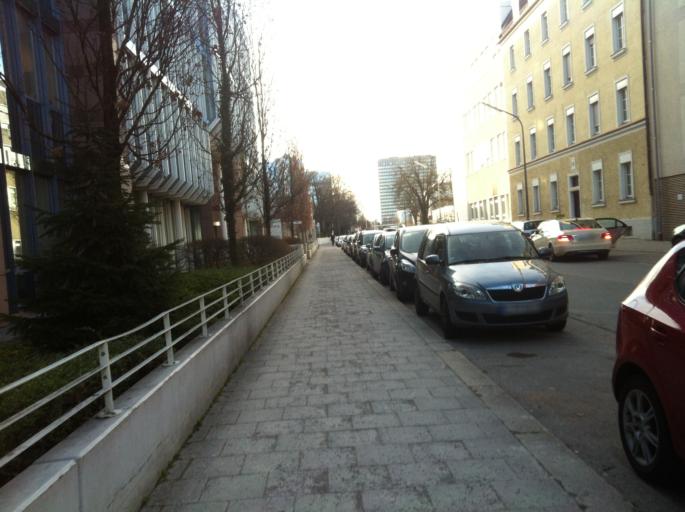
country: DE
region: Bavaria
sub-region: Upper Bavaria
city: Pullach im Isartal
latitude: 48.0974
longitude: 11.5328
